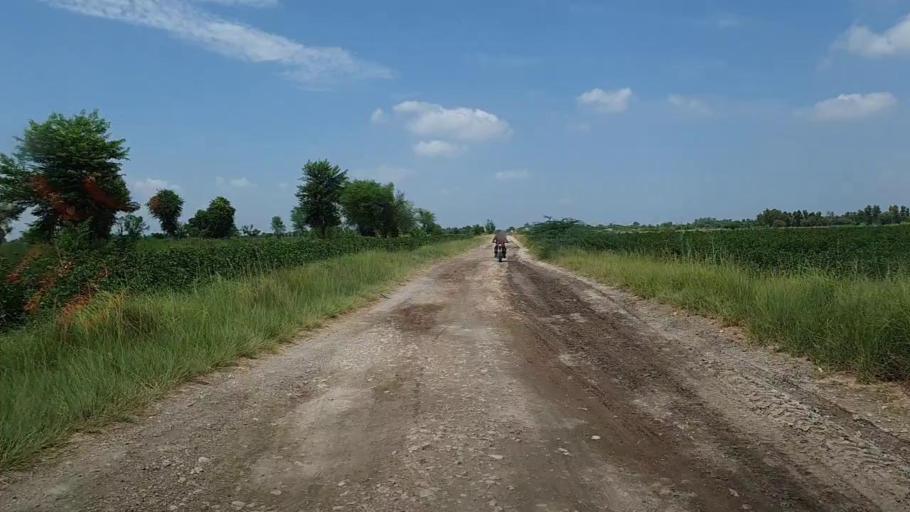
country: PK
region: Sindh
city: Bhiria
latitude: 26.9694
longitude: 68.2384
